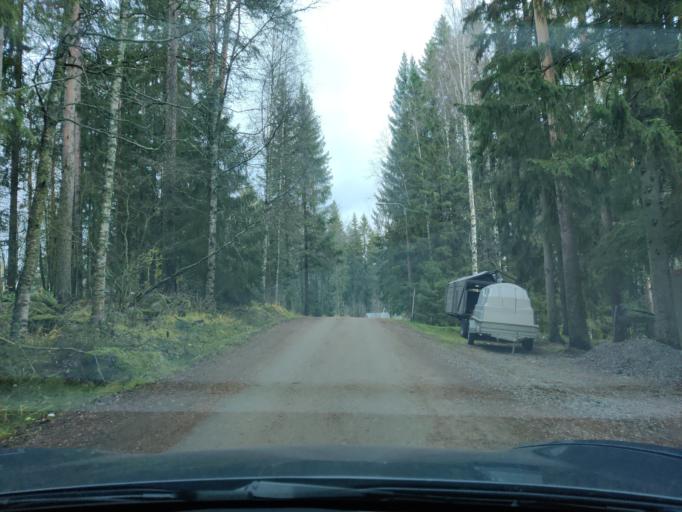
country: FI
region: Northern Savo
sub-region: Ylae-Savo
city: Kiuruvesi
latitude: 63.6444
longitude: 26.6441
